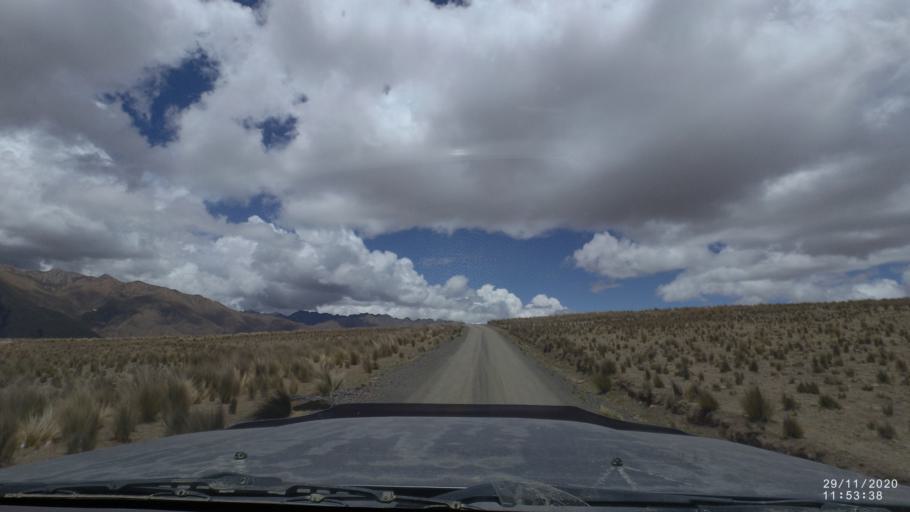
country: BO
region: Cochabamba
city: Cochabamba
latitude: -17.1651
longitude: -66.2691
